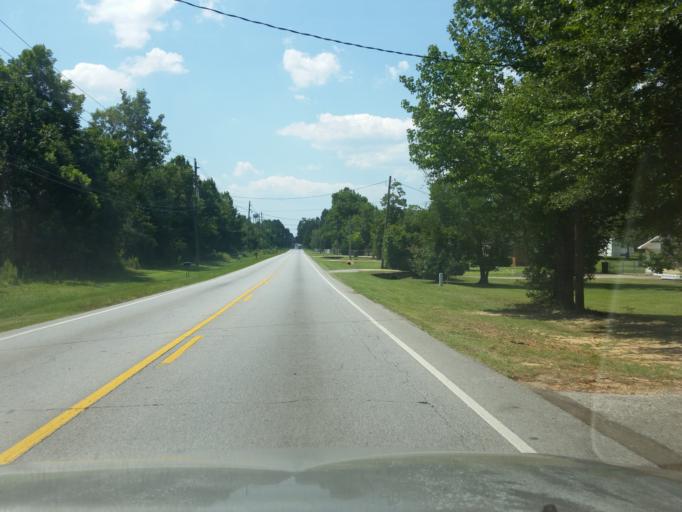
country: US
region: Florida
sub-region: Escambia County
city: Cantonment
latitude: 30.6421
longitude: -87.3178
